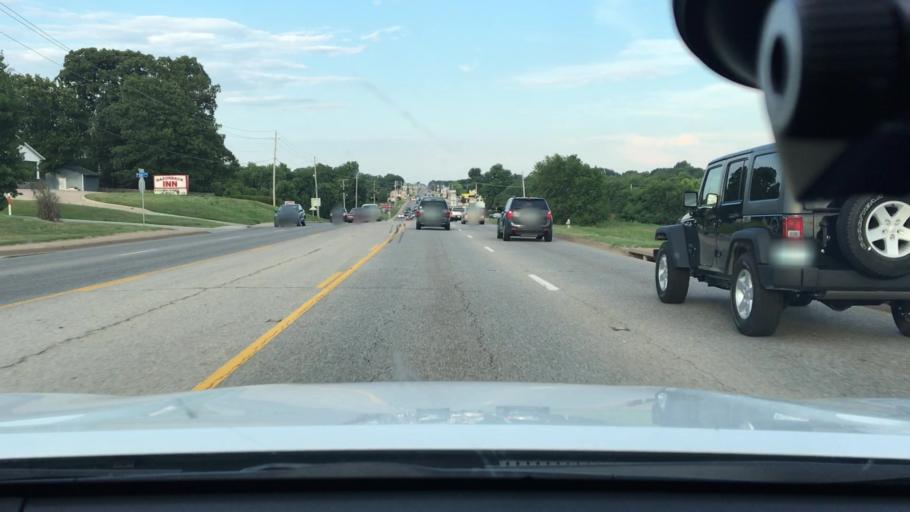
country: US
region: Arkansas
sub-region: Benton County
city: Rogers
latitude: 36.3345
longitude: -94.1650
